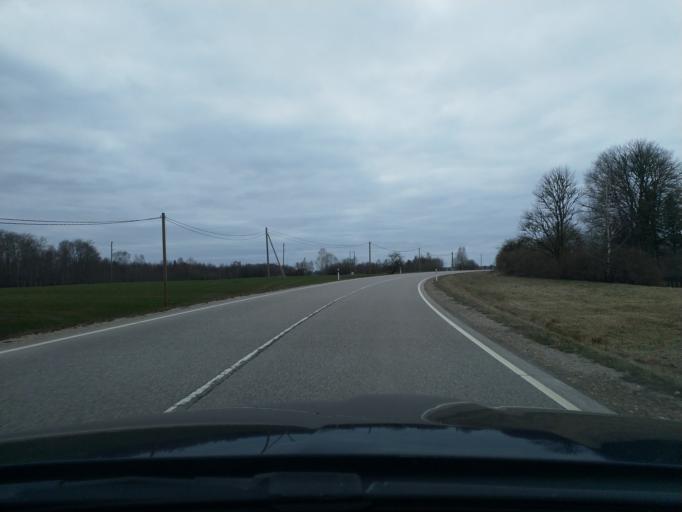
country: LV
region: Talsu Rajons
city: Sabile
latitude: 56.9305
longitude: 22.5236
